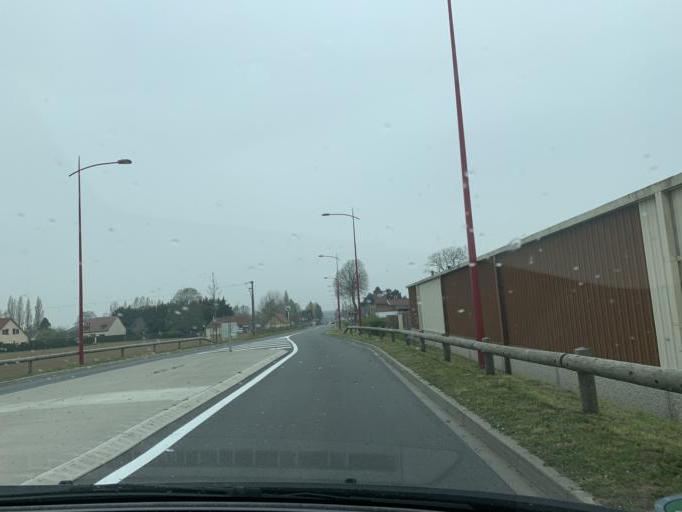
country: FR
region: Picardie
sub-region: Departement de la Somme
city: Nouvion
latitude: 50.1702
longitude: 1.8112
